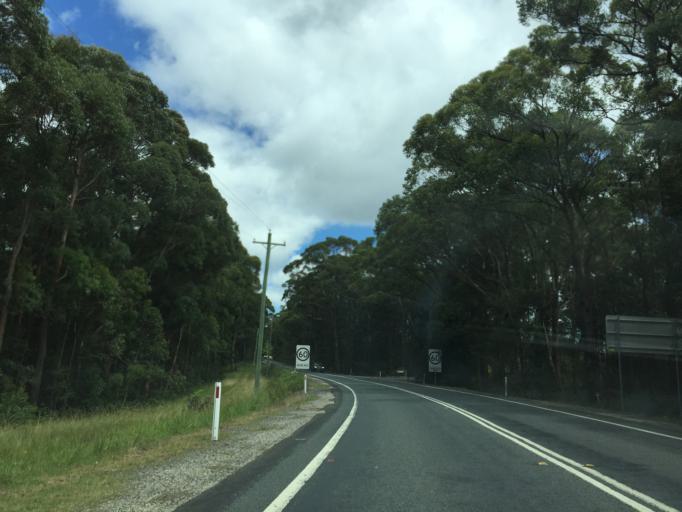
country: AU
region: New South Wales
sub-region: Hawkesbury
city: Richmond
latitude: -33.5095
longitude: 150.5663
